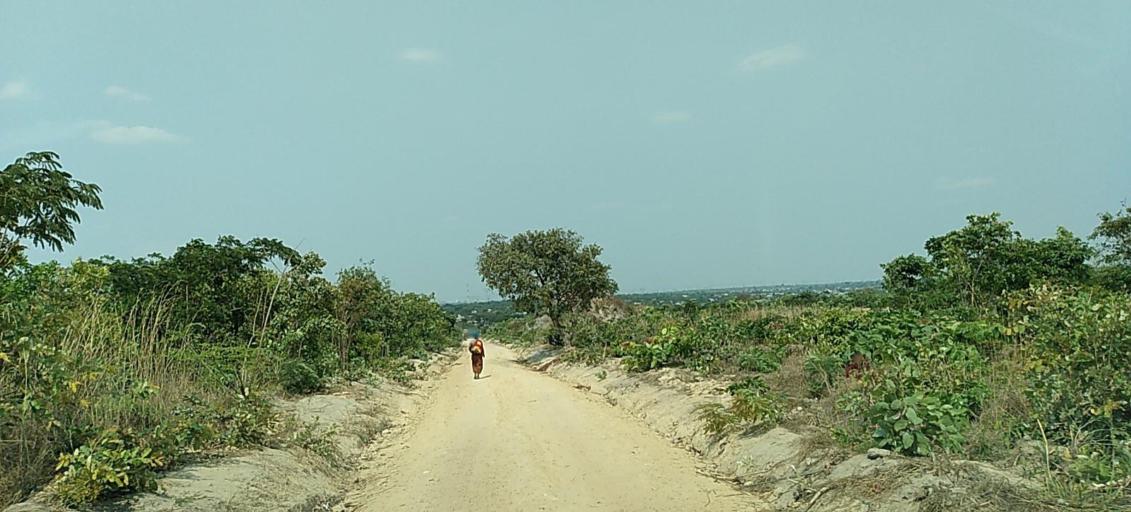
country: ZM
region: Copperbelt
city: Chambishi
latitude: -12.6230
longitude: 28.0847
